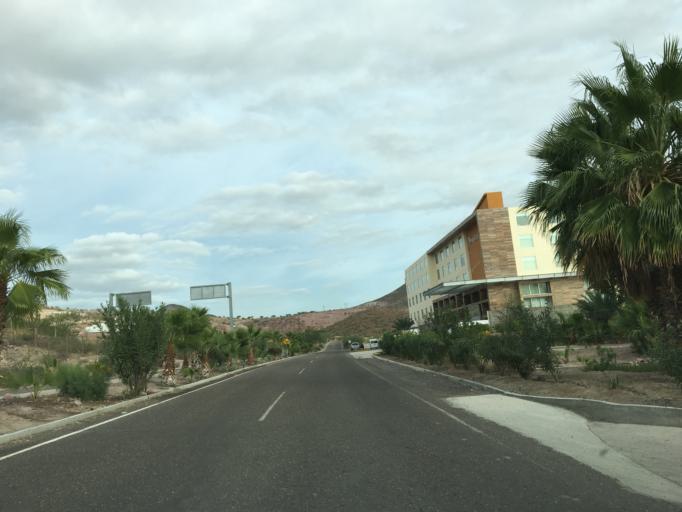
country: MX
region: Baja California Sur
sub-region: La Paz
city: La Paz
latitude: 24.2196
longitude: -110.3039
